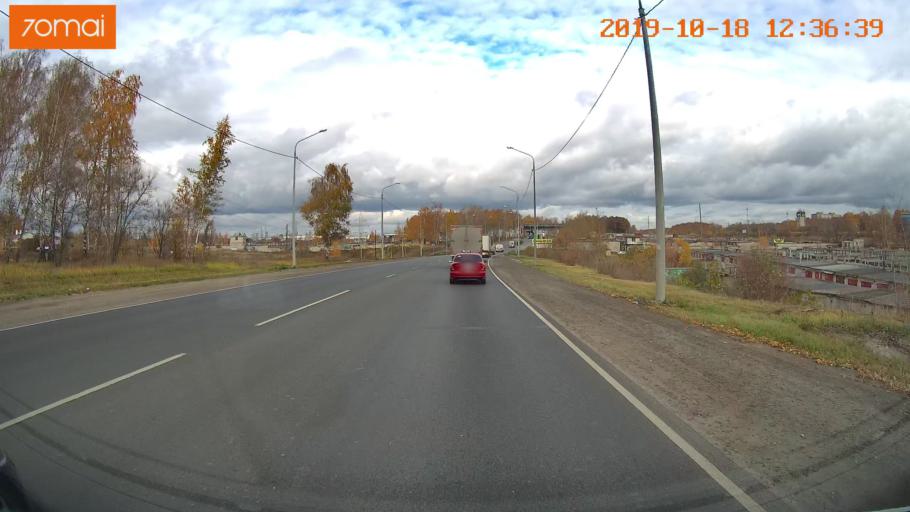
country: RU
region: Rjazan
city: Ryazan'
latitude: 54.6371
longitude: 39.6345
